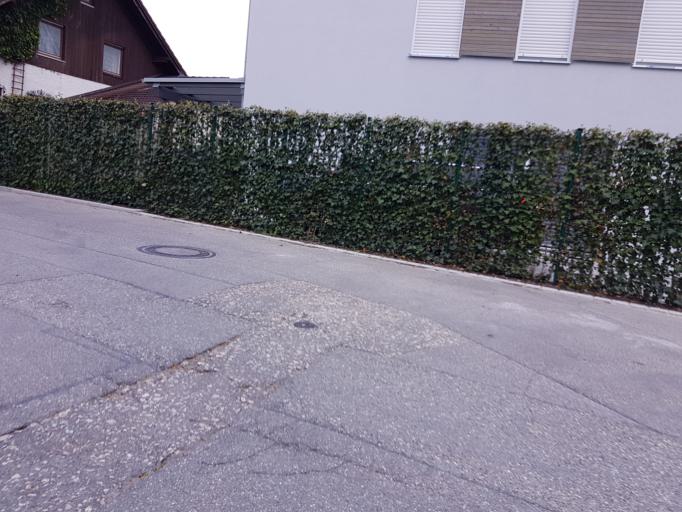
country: DE
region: Bavaria
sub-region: Upper Bavaria
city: Karlsfeld
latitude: 48.2107
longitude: 11.4556
